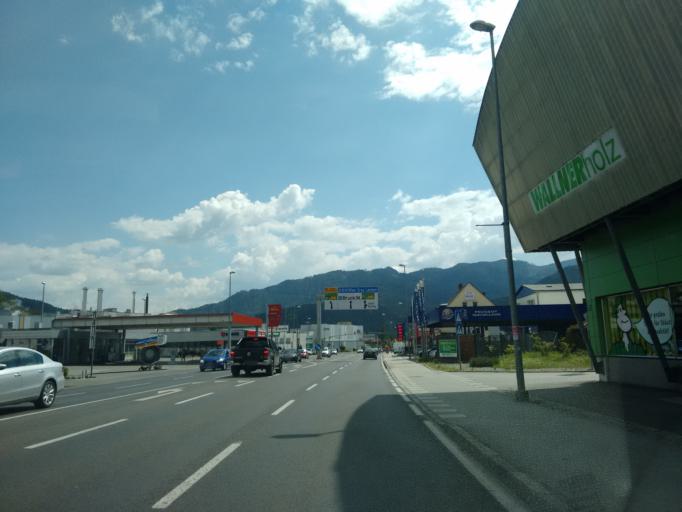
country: AT
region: Styria
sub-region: Politischer Bezirk Bruck-Muerzzuschlag
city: Bruck an der Mur
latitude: 47.4197
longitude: 15.2743
